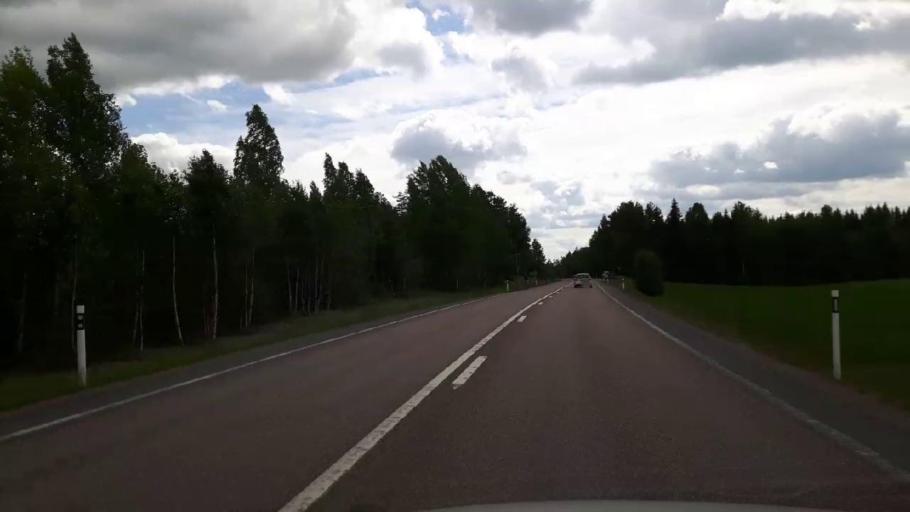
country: SE
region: Dalarna
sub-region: Saters Kommun
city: Saeter
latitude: 60.4682
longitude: 15.7978
